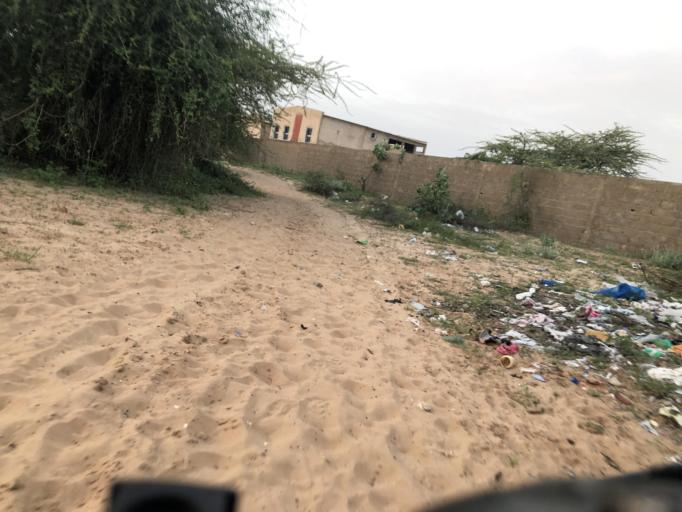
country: SN
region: Saint-Louis
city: Saint-Louis
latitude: 16.0625
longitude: -16.4328
